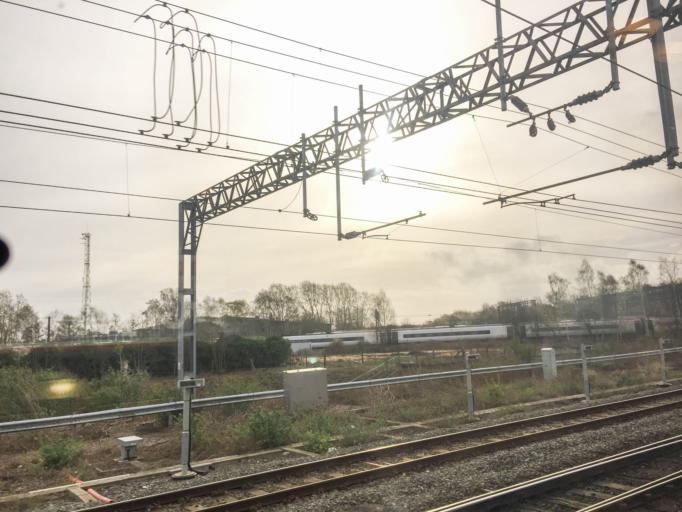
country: GB
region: England
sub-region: Cheshire East
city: Crewe
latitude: 53.0941
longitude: -2.4352
